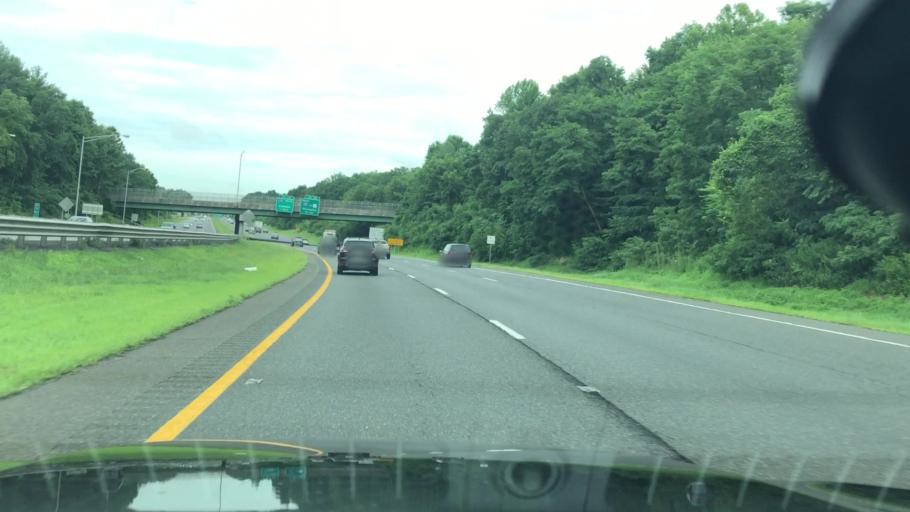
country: US
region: New Jersey
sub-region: Mercer County
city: White Horse
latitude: 40.1859
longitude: -74.7022
